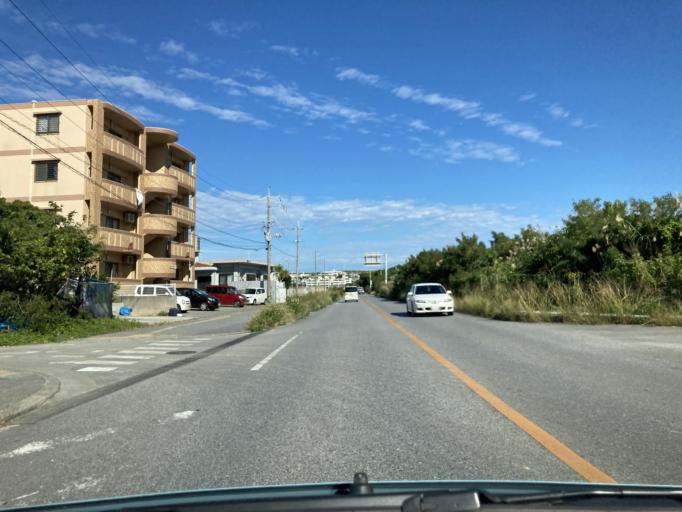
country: JP
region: Okinawa
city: Okinawa
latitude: 26.3727
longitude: 127.7461
